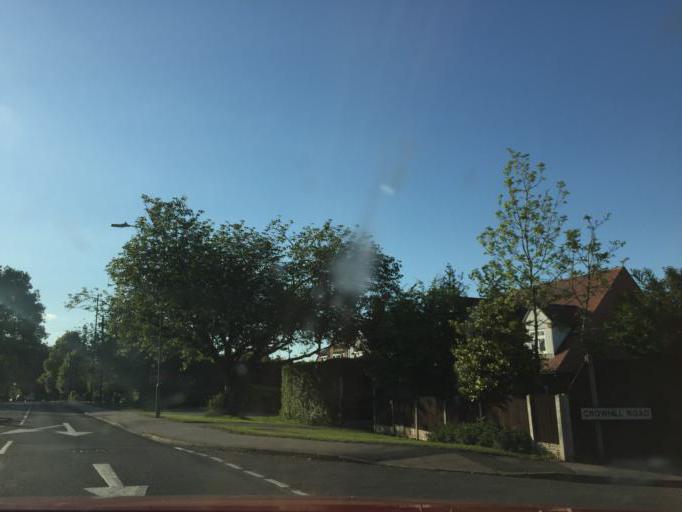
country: GB
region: England
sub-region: Warwickshire
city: Attleborough
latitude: 52.5073
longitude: -1.4406
